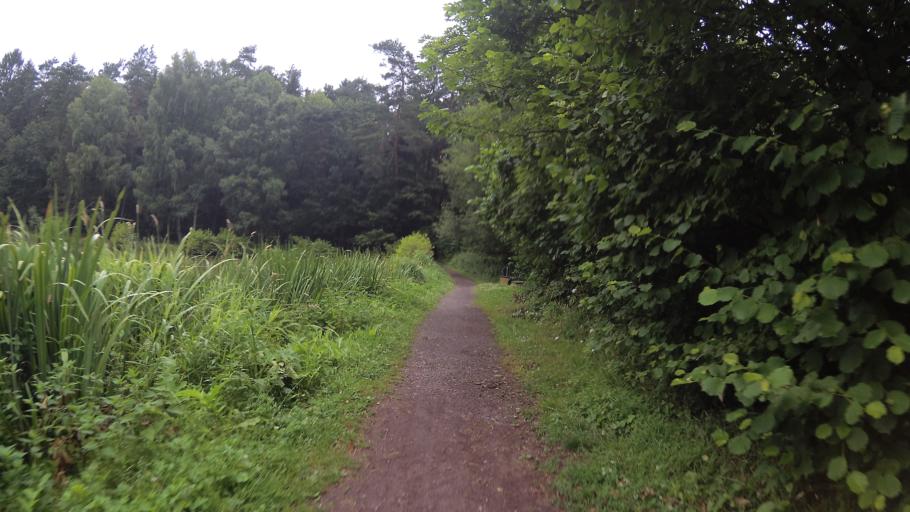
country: DE
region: Saarland
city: Homburg
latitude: 49.3129
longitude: 7.3755
